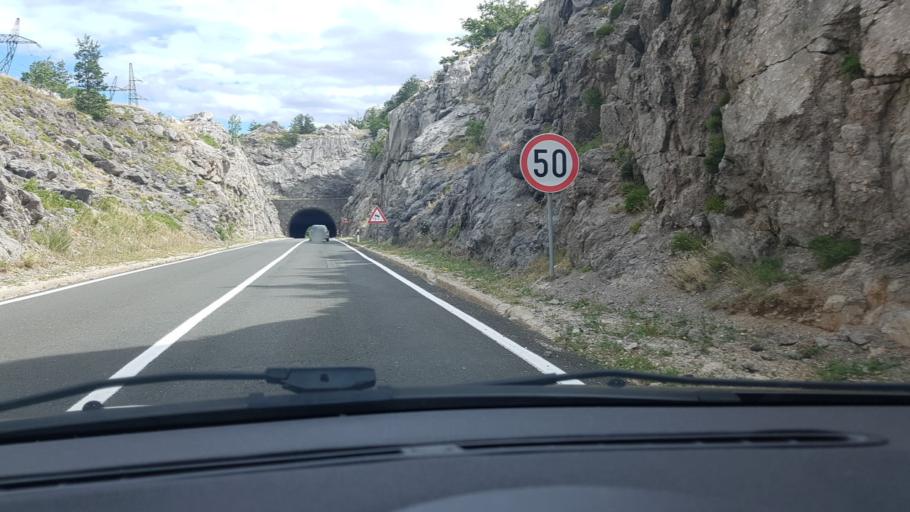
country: HR
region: Zadarska
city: Gracac
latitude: 44.2496
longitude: 15.8081
